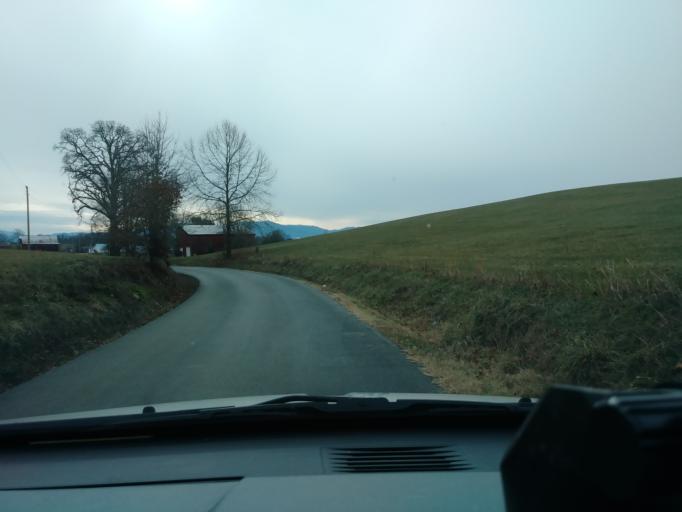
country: US
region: Tennessee
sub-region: Greene County
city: Greeneville
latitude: 36.0916
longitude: -82.8943
